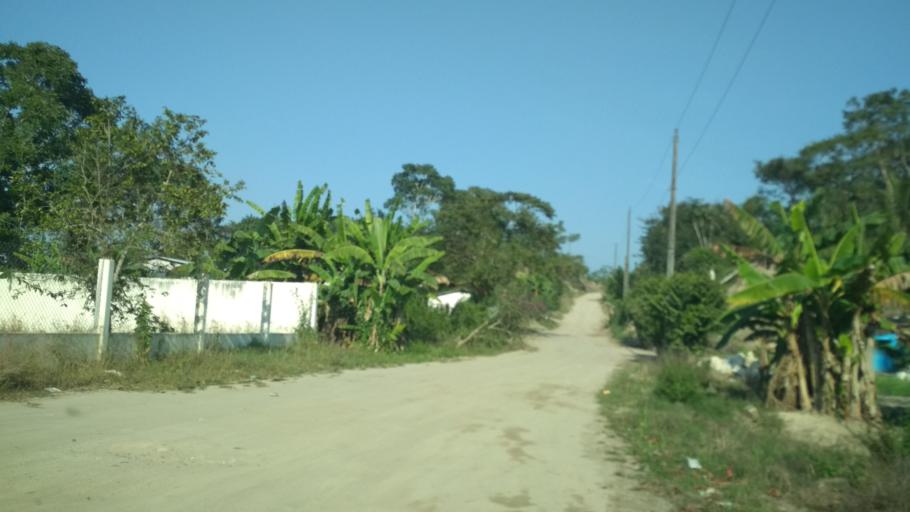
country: MX
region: Puebla
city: San Jose Acateno
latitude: 20.1903
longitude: -97.2667
